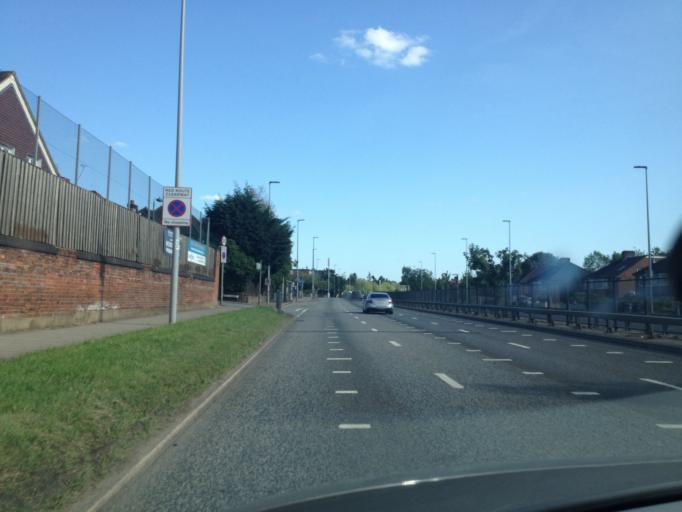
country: GB
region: England
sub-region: Greater London
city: Hendon
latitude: 51.5717
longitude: -0.2104
